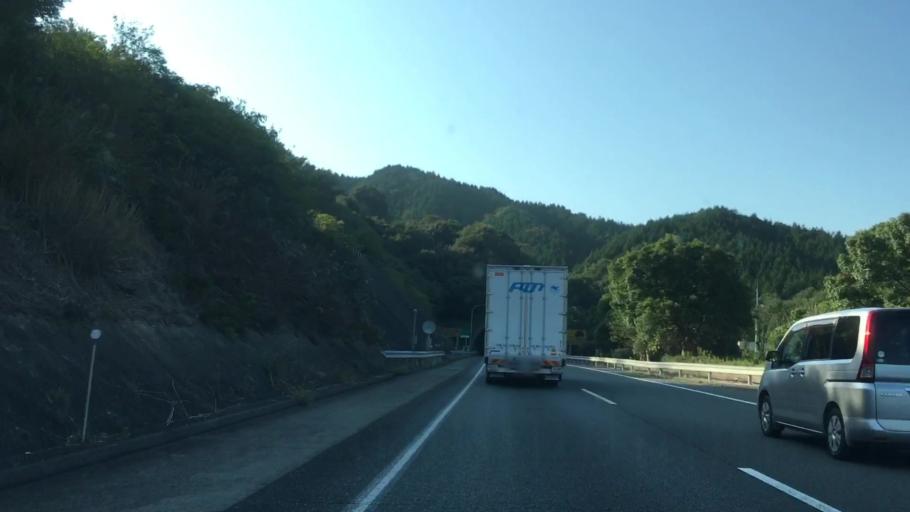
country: JP
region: Yamaguchi
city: Hofu
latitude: 34.0780
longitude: 131.4884
